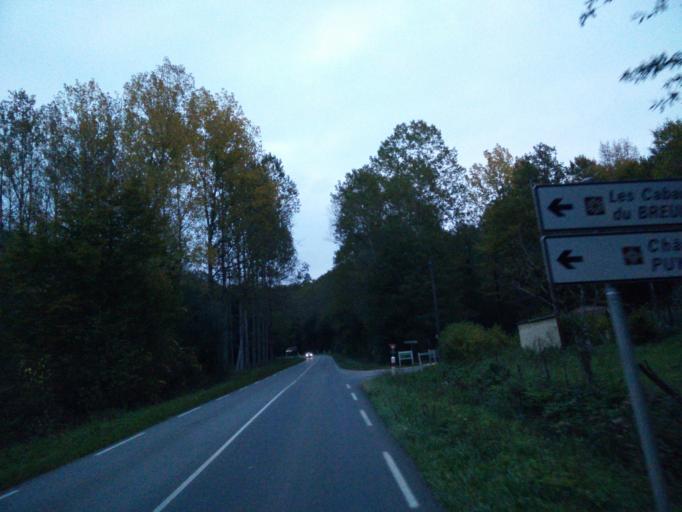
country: FR
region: Aquitaine
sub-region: Departement de la Dordogne
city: Sarlat-la-Caneda
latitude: 44.9084
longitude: 1.1404
